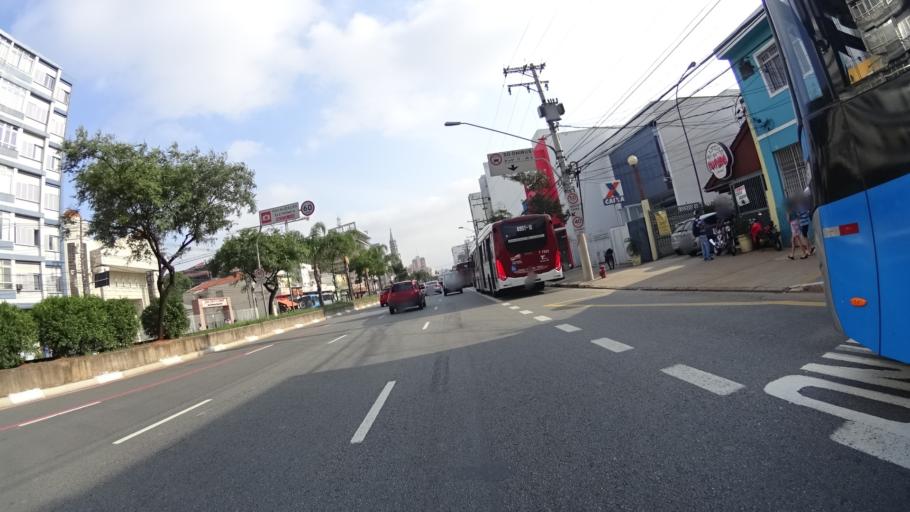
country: BR
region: Sao Paulo
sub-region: Sao Paulo
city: Sao Paulo
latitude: -23.5937
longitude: -46.6367
